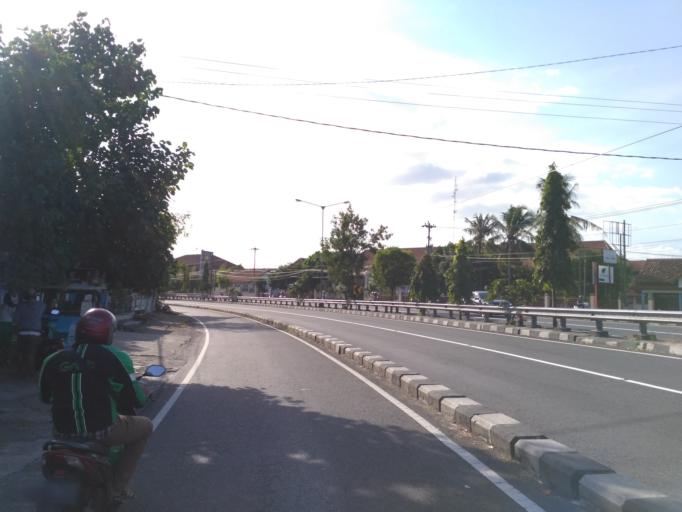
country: ID
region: Daerah Istimewa Yogyakarta
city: Depok
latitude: -7.7667
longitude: 110.4311
